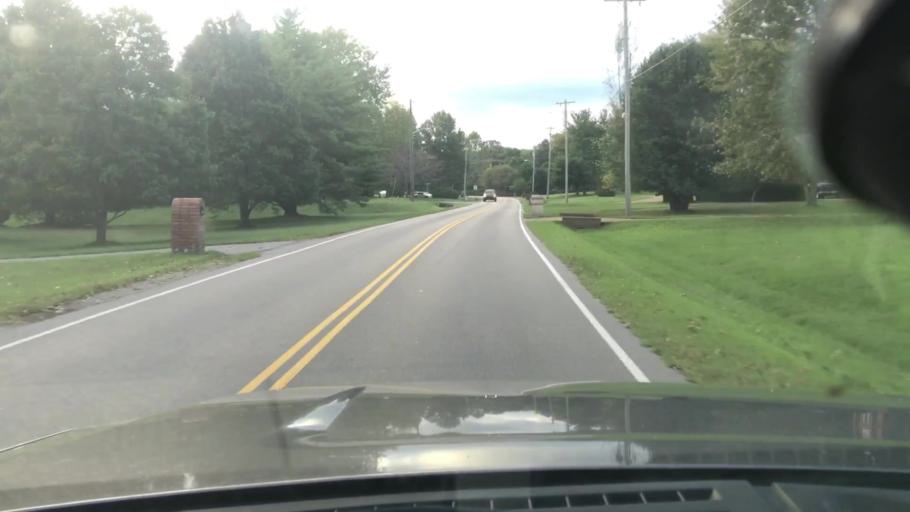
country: US
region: Tennessee
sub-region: Davidson County
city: Forest Hills
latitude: 36.0287
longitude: -86.8298
